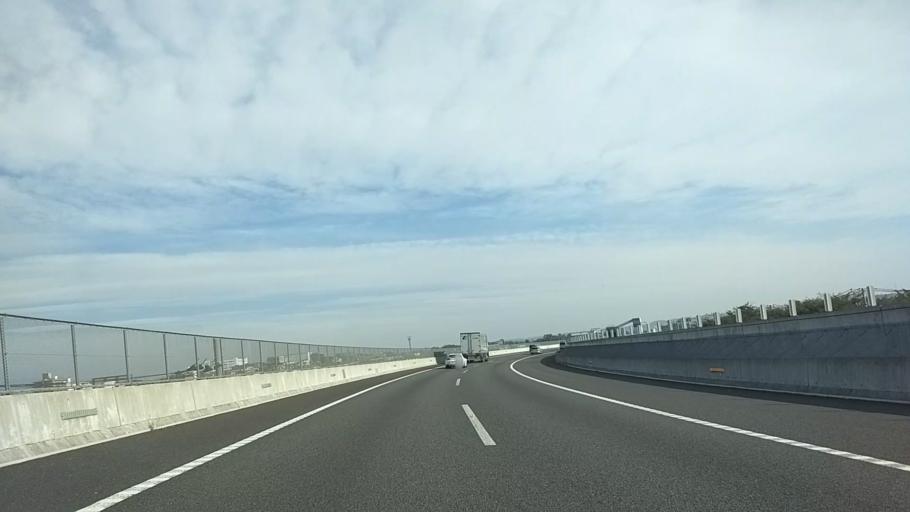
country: JP
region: Kanagawa
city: Atsugi
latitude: 35.4573
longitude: 139.3721
